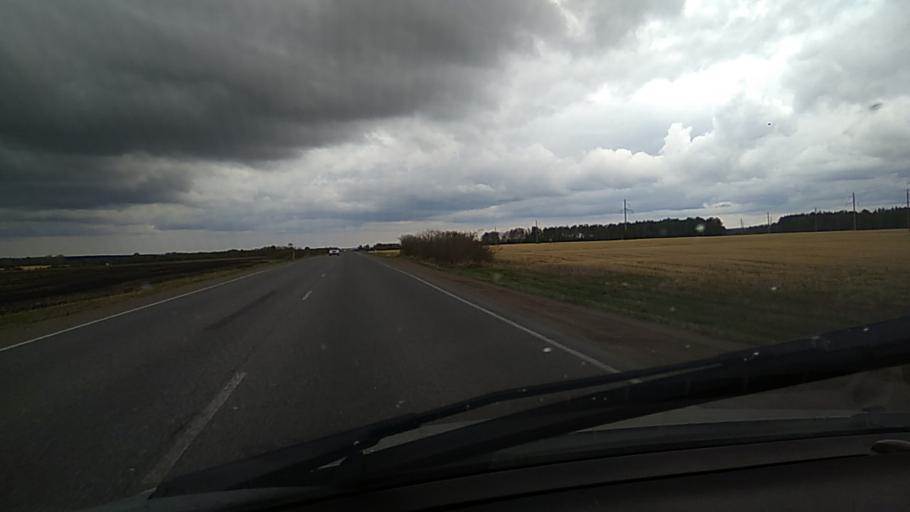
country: RU
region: Kurgan
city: Dalmatovo
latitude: 56.2898
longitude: 62.8676
